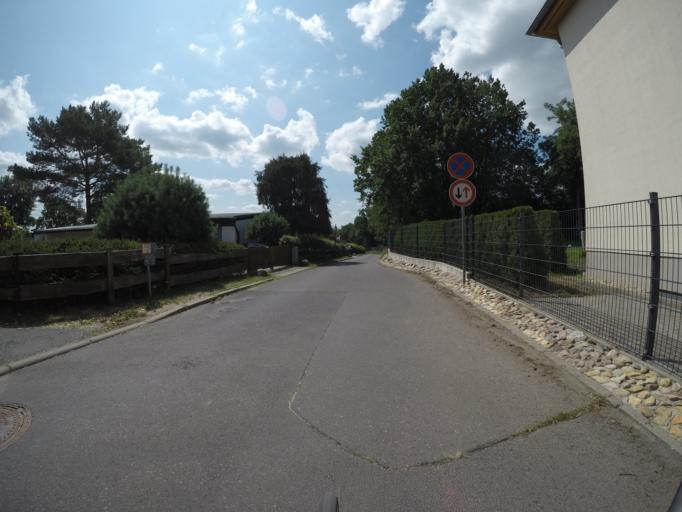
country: DE
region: Brandenburg
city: Werder
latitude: 52.4084
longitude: 12.9859
